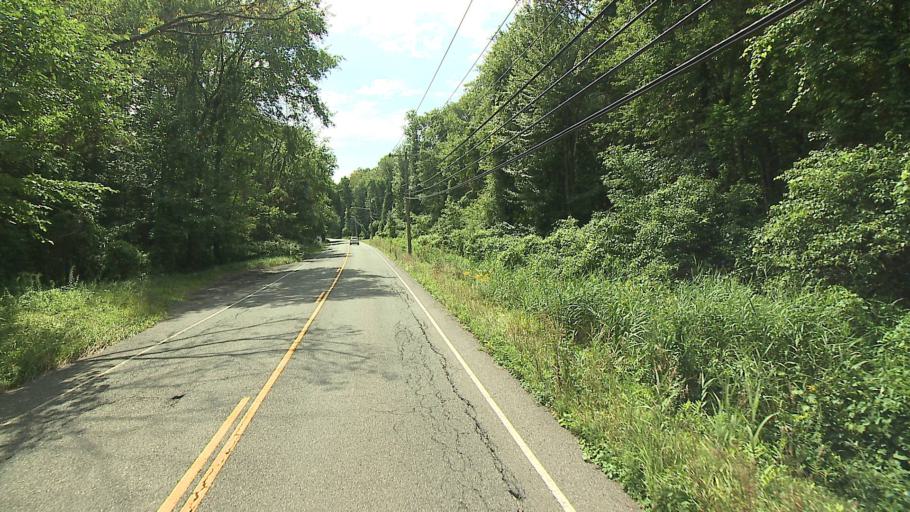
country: US
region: Connecticut
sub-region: Fairfield County
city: Sherman
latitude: 41.5684
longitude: -73.4971
